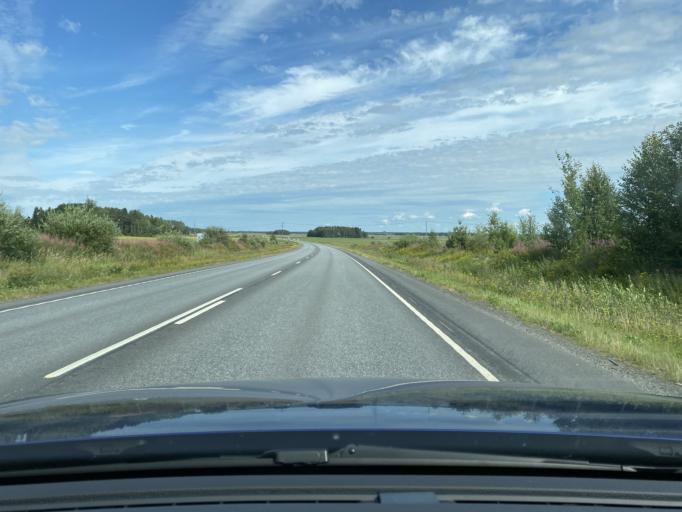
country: FI
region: Southern Ostrobothnia
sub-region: Seinaejoki
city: Ylihaermae
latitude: 63.1701
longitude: 22.8073
